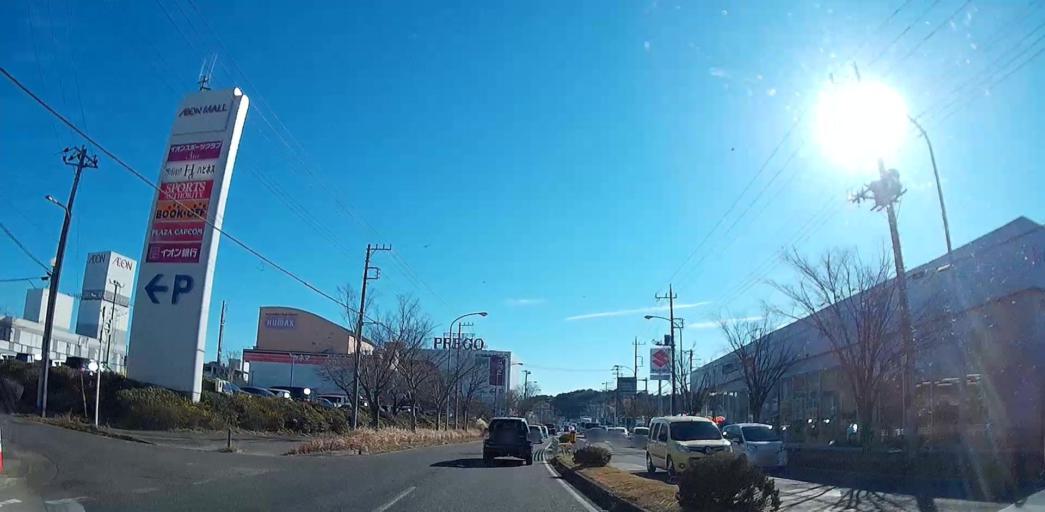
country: JP
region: Chiba
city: Narita
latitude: 35.7942
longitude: 140.3192
